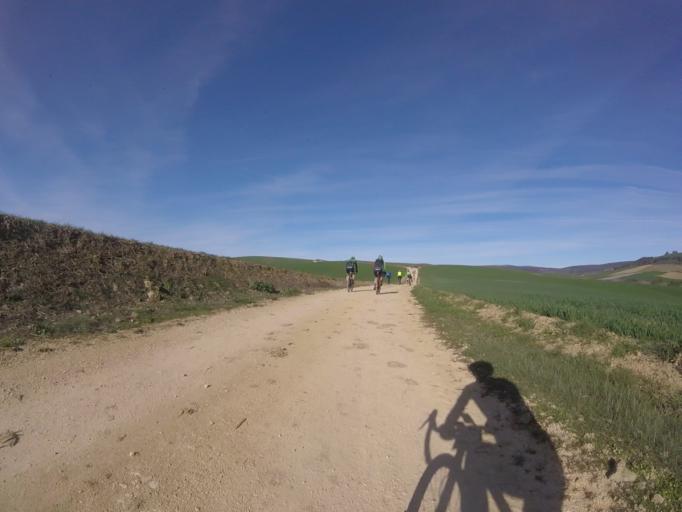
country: ES
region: Navarre
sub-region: Provincia de Navarra
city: Yerri
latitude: 42.7193
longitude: -1.9631
